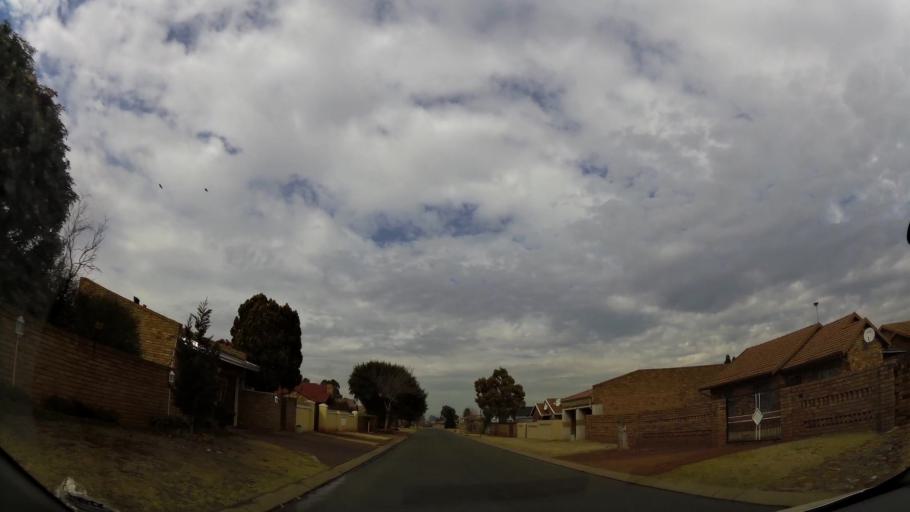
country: ZA
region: Gauteng
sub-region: Ekurhuleni Metropolitan Municipality
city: Germiston
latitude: -26.3298
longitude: 28.1783
